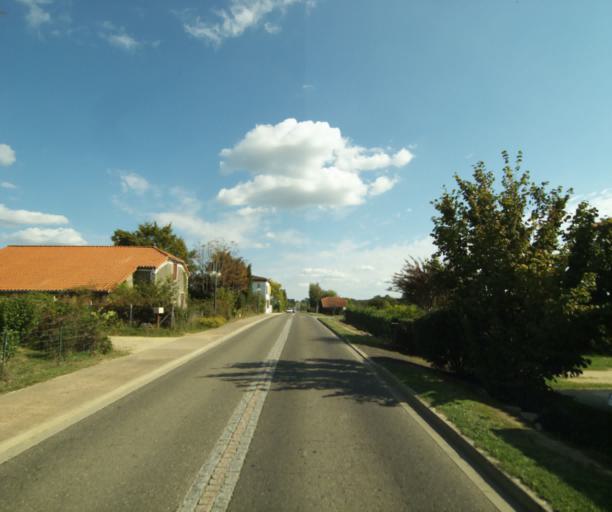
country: FR
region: Midi-Pyrenees
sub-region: Departement du Gers
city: Cazaubon
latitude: 43.9342
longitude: -0.0590
